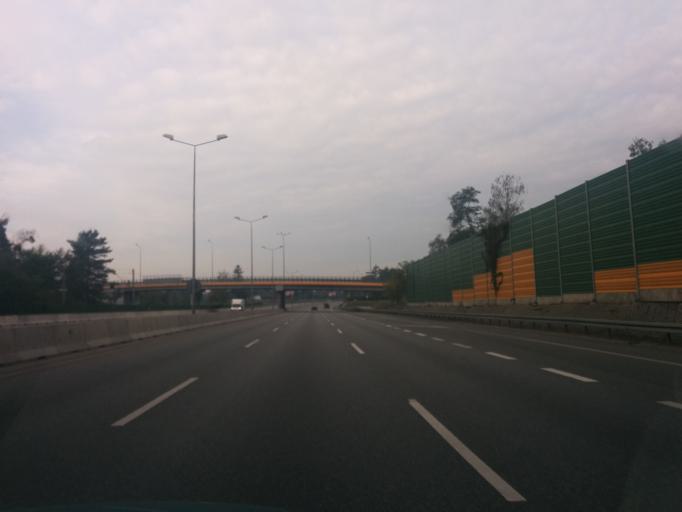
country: PL
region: Masovian Voivodeship
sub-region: Warszawa
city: Bemowo
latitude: 52.2509
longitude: 20.9401
